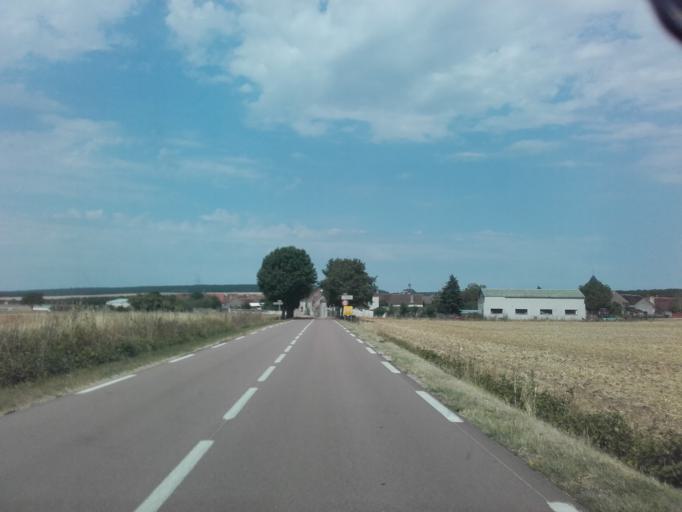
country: FR
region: Bourgogne
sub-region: Departement de l'Yonne
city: Joux-la-Ville
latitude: 47.7251
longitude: 3.8534
